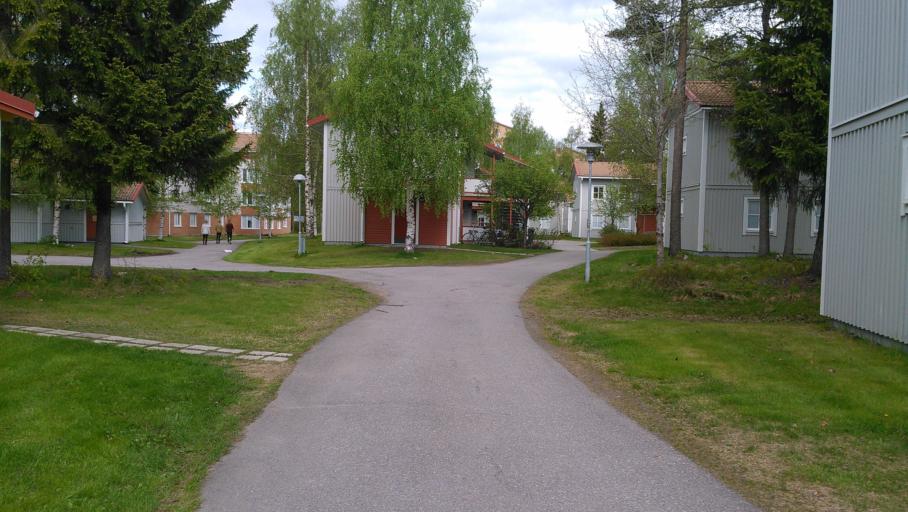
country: SE
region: Vaesterbotten
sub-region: Umea Kommun
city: Ersmark
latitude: 63.8240
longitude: 20.3288
